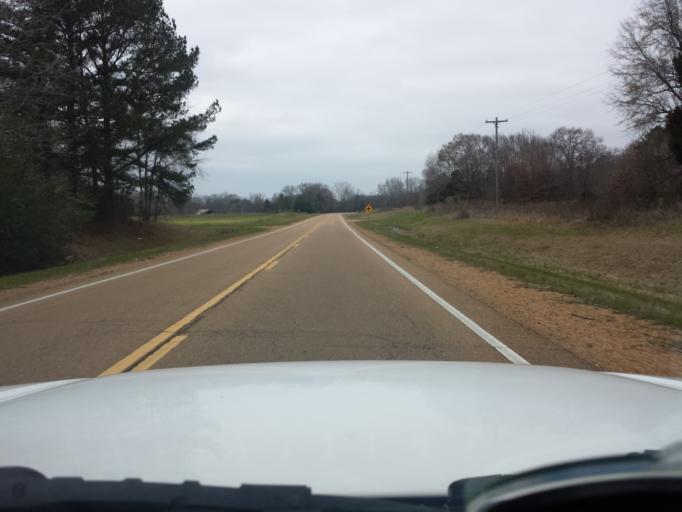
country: US
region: Mississippi
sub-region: Madison County
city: Canton
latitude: 32.7466
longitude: -90.1402
